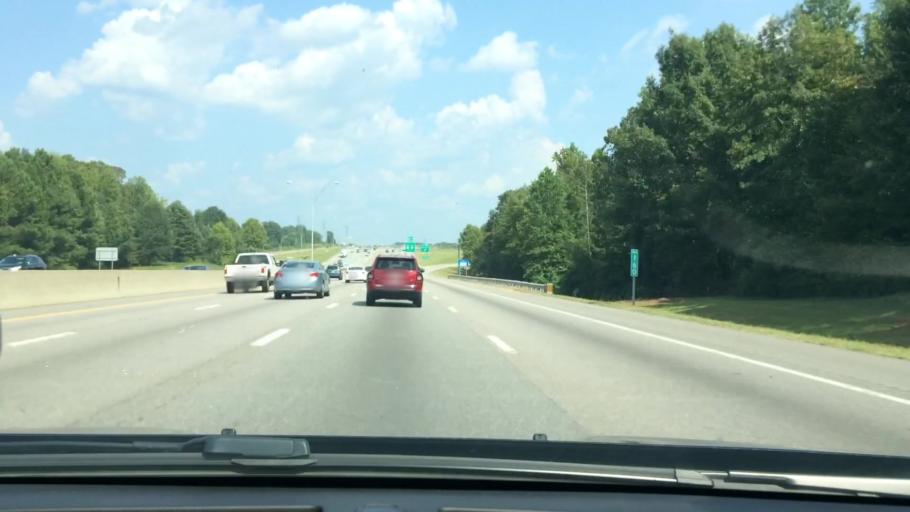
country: US
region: North Carolina
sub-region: Orange County
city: Hillsborough
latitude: 36.0775
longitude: -79.1776
